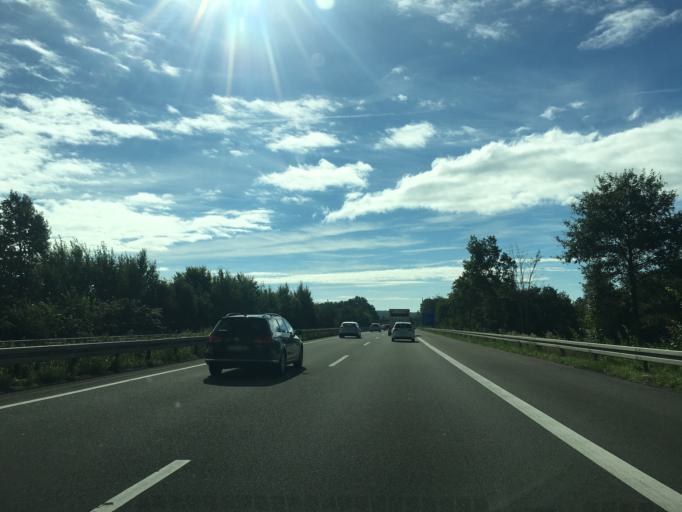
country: DE
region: Lower Saxony
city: Melle
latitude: 52.2023
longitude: 8.3070
